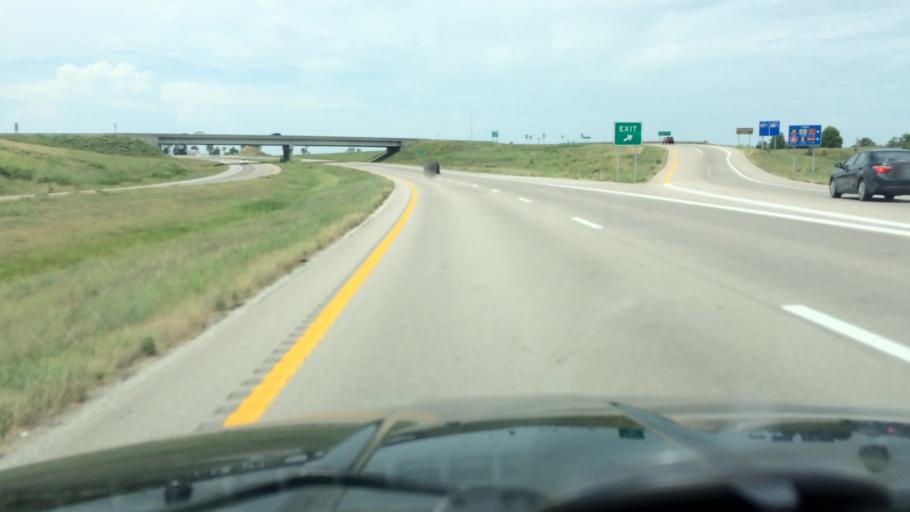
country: US
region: Missouri
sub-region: Polk County
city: Bolivar
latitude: 37.5729
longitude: -93.3970
